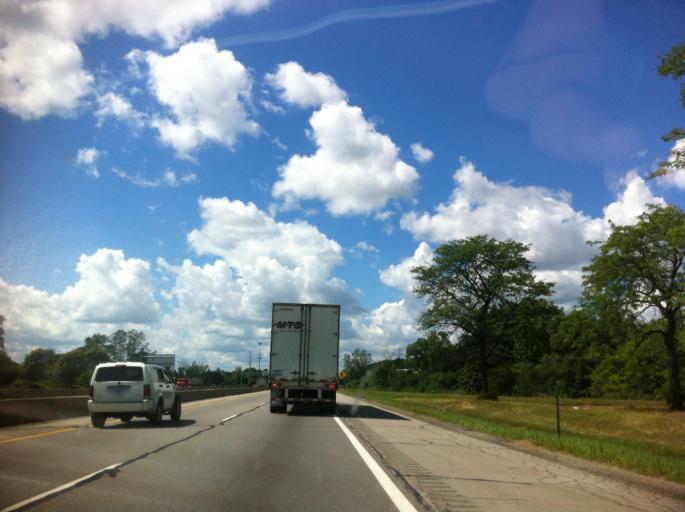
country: US
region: Michigan
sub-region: Washtenaw County
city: Ann Arbor
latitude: 42.2268
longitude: -83.6881
